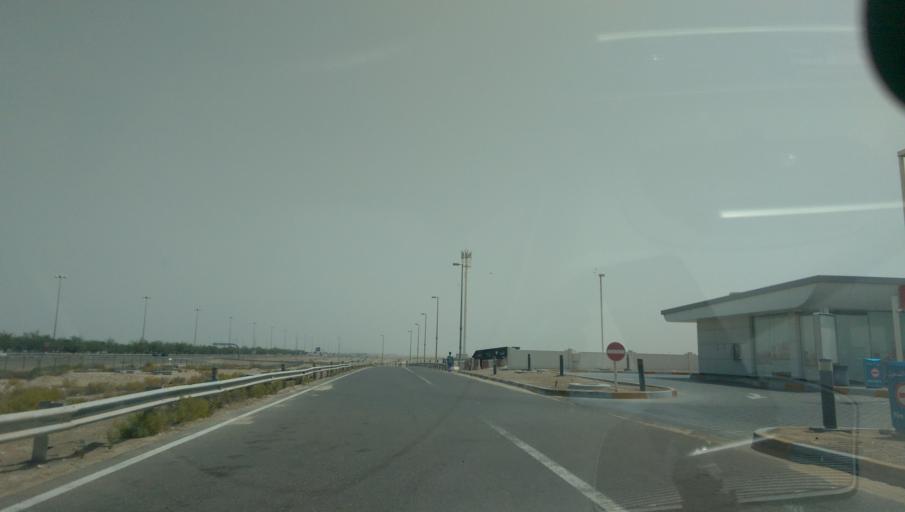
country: AE
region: Abu Dhabi
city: Abu Dhabi
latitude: 24.3870
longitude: 54.6639
